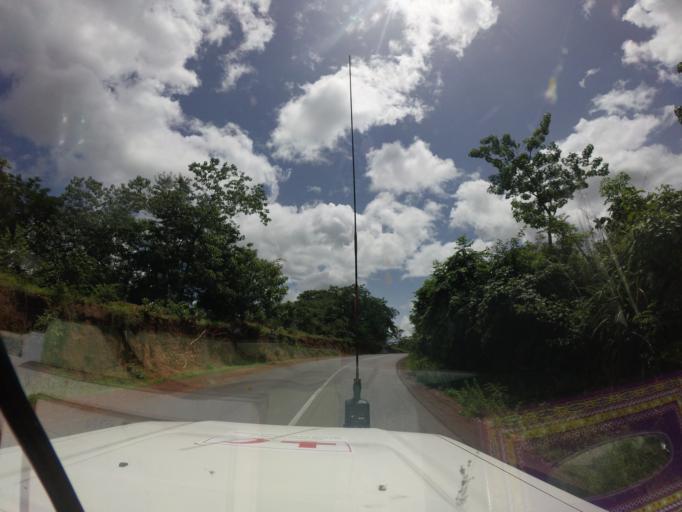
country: SL
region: Northern Province
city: Bindi
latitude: 10.1697
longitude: -11.4006
